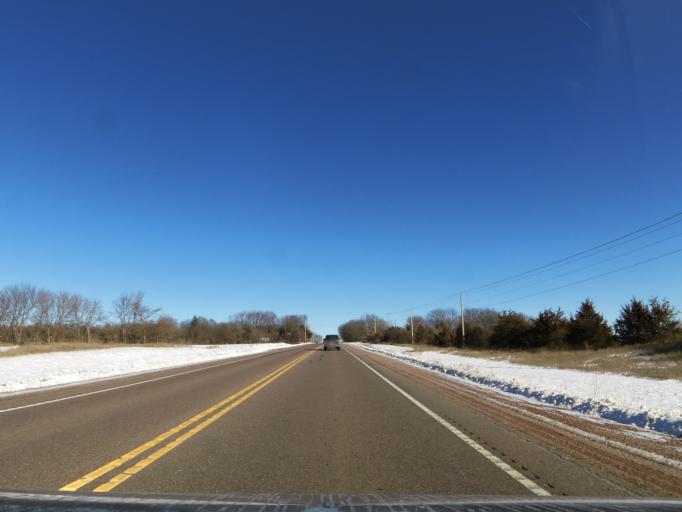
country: US
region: Wisconsin
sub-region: Sauk County
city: Baraboo
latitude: 43.4753
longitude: -89.6538
